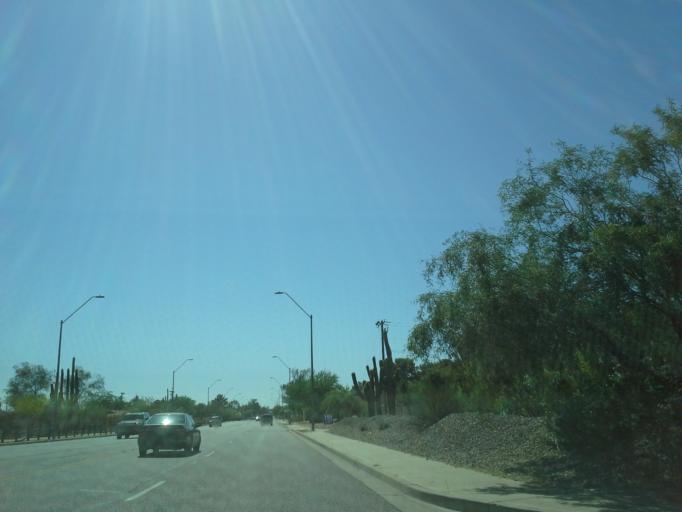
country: US
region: Arizona
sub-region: Maricopa County
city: Paradise Valley
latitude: 33.5968
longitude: -111.9374
